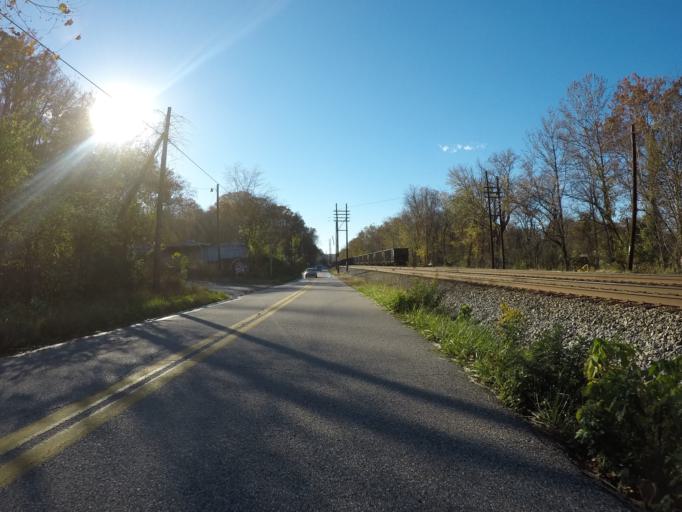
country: US
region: Ohio
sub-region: Lawrence County
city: Burlington
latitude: 38.3947
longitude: -82.5396
